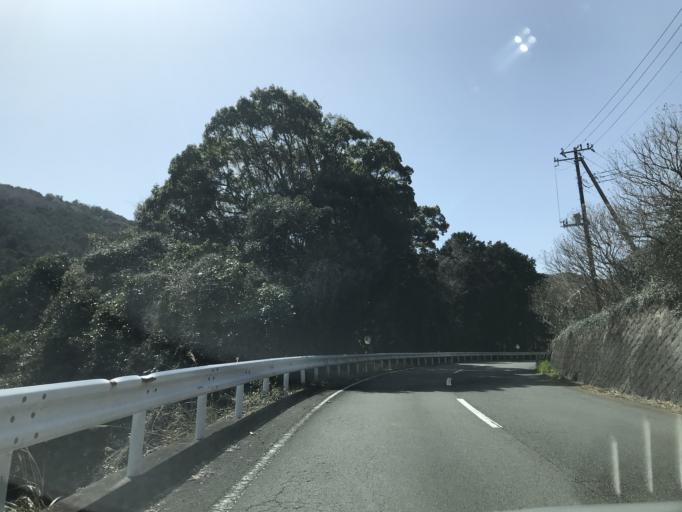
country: JP
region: Shizuoka
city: Heda
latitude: 35.0083
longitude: 138.8338
